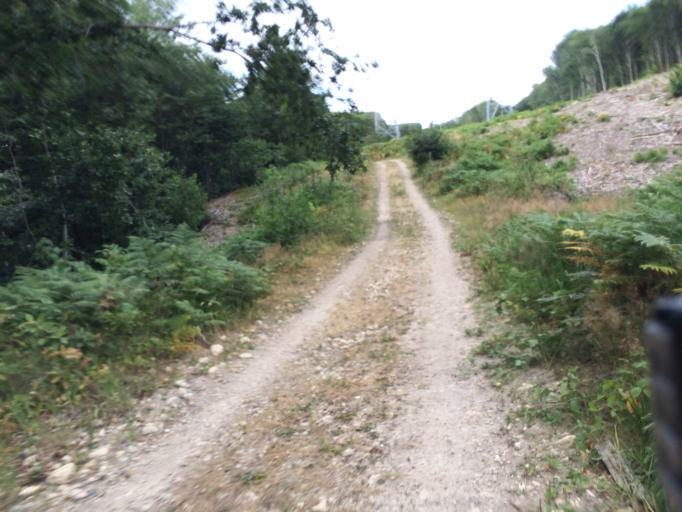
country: FR
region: Ile-de-France
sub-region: Departement de l'Essonne
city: Bievres
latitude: 48.7593
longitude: 2.2259
